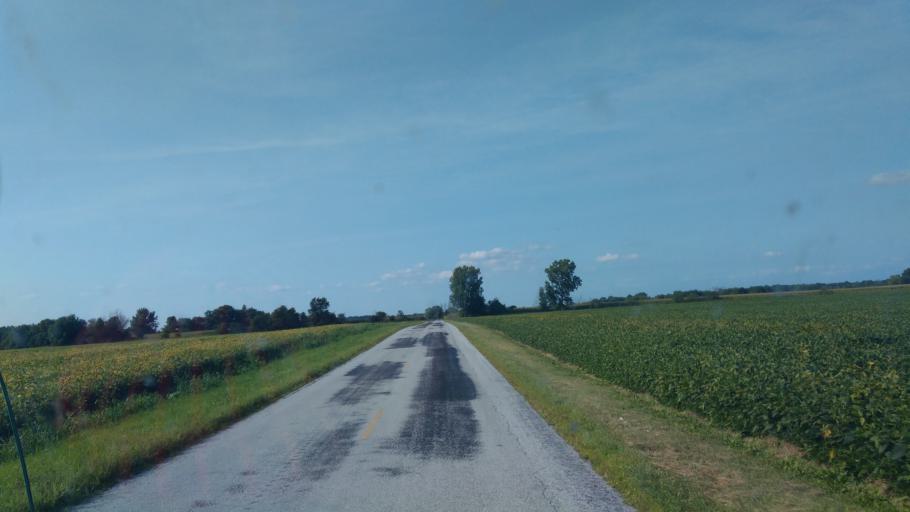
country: US
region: Ohio
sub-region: Hardin County
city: Kenton
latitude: 40.7282
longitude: -83.5735
